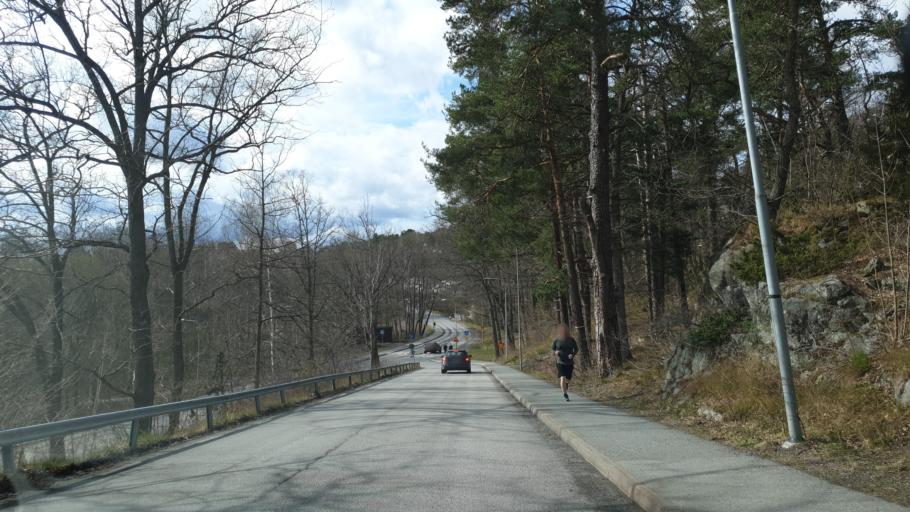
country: SE
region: Stockholm
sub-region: Nacka Kommun
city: Saltsjobaden
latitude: 59.2699
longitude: 18.3046
